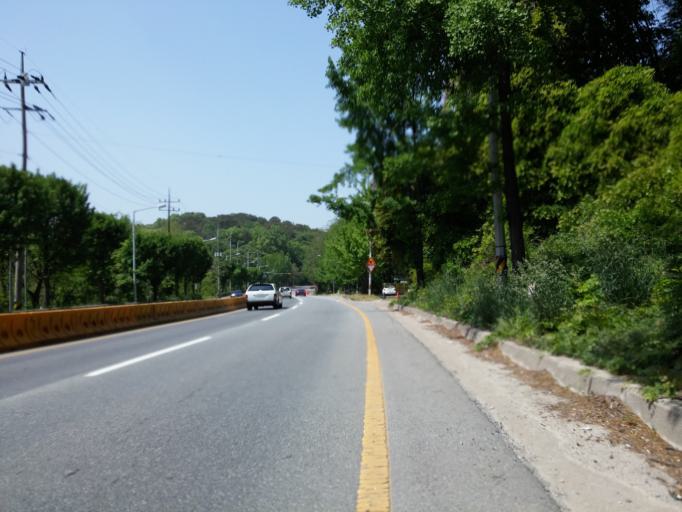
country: KR
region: Daejeon
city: Daejeon
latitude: 36.2812
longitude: 127.3024
